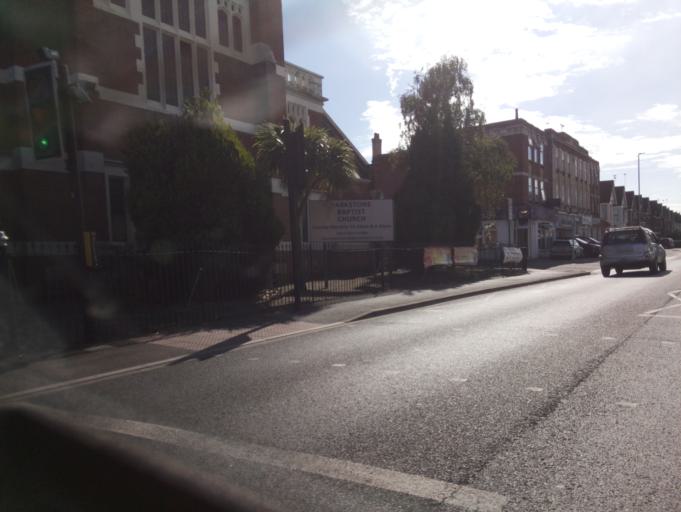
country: GB
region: England
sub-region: Dorset
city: Parkstone
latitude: 50.7283
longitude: -1.9299
